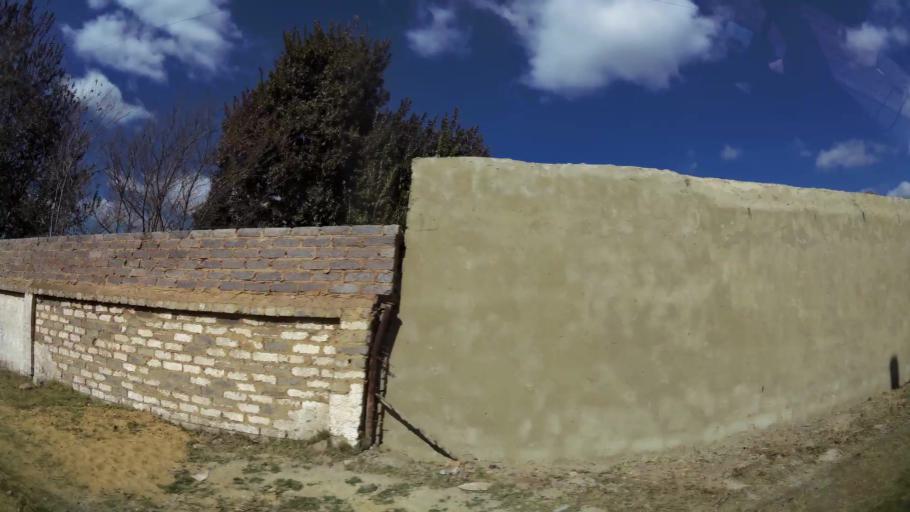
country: ZA
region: Gauteng
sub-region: West Rand District Municipality
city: Krugersdorp
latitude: -26.1378
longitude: 27.7966
